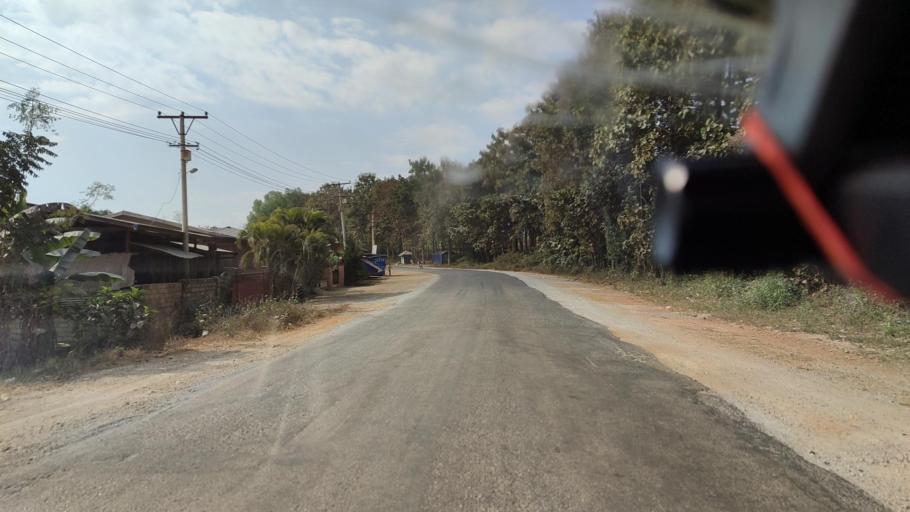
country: MM
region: Shan
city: Lashio
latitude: 23.2467
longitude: 97.9233
